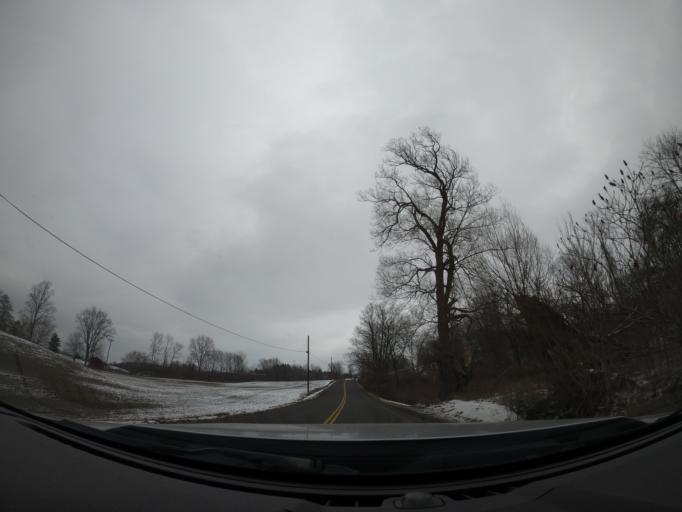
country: US
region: New York
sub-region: Cayuga County
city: Moravia
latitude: 42.7350
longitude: -76.3927
